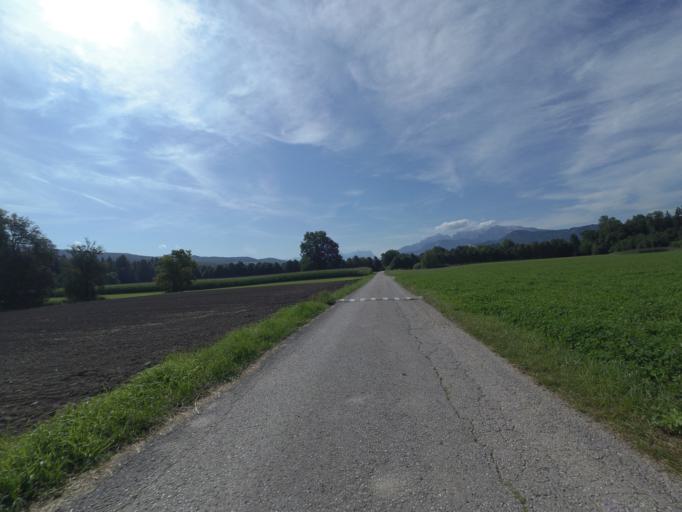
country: AT
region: Salzburg
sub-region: Politischer Bezirk Salzburg-Umgebung
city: Anif
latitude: 47.7495
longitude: 13.0725
